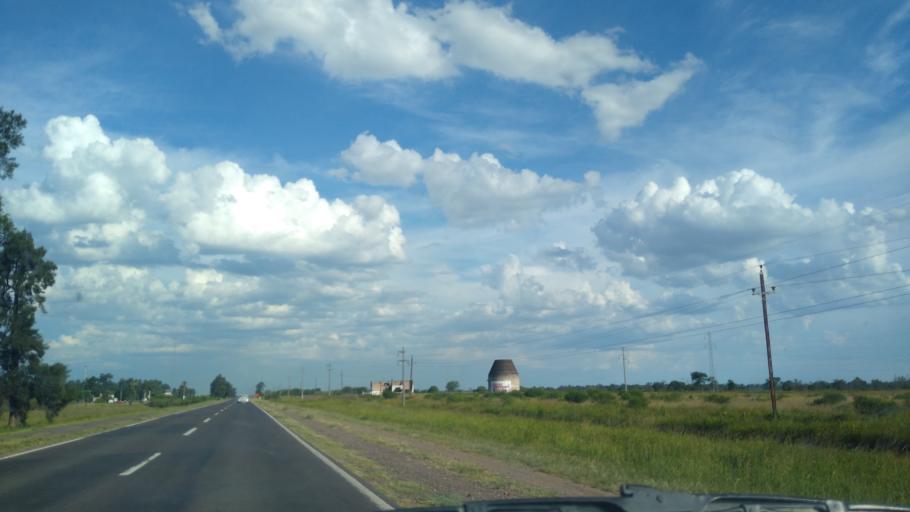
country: AR
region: Chaco
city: Presidencia Roque Saenz Pena
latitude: -26.8214
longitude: -60.3933
